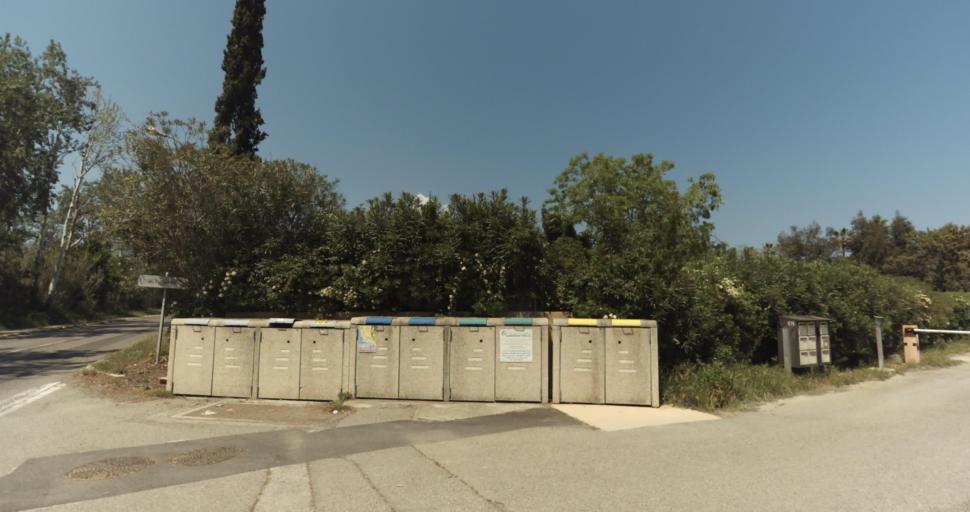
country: FR
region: Corsica
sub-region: Departement de la Haute-Corse
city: Biguglia
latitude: 42.6353
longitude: 9.4622
